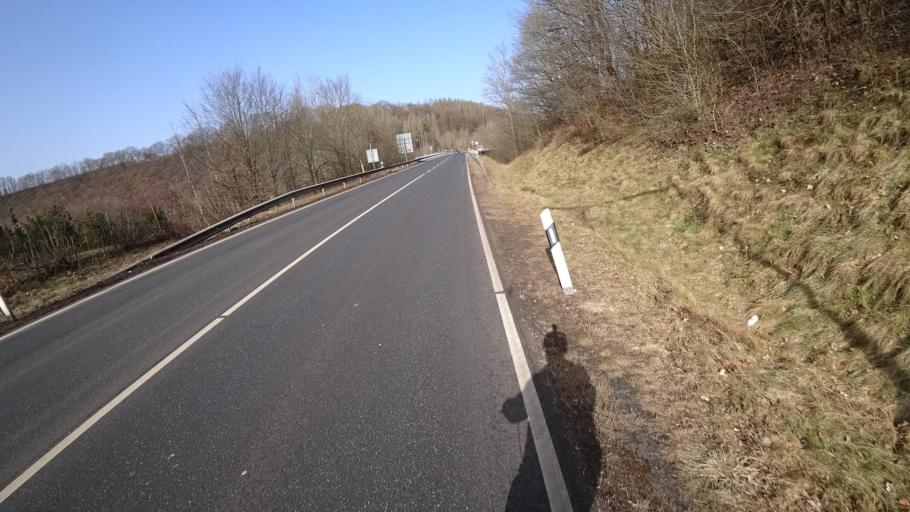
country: DE
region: Rheinland-Pfalz
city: Wissen
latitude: 50.7751
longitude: 7.7148
